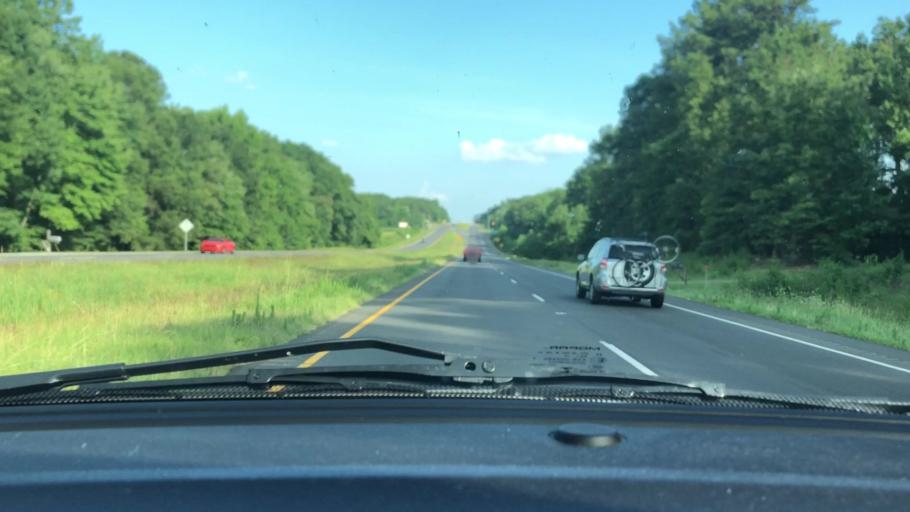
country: US
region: North Carolina
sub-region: Chatham County
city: Siler City
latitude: 35.6355
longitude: -79.3728
